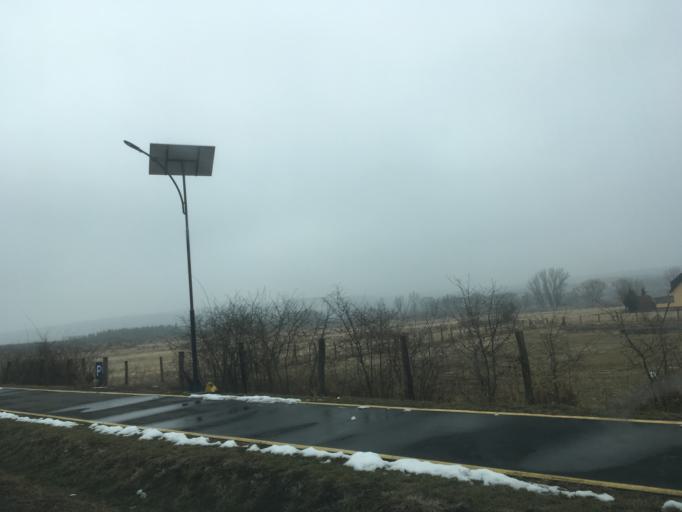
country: HU
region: Heves
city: Egerszalok
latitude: 47.8634
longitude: 20.3279
